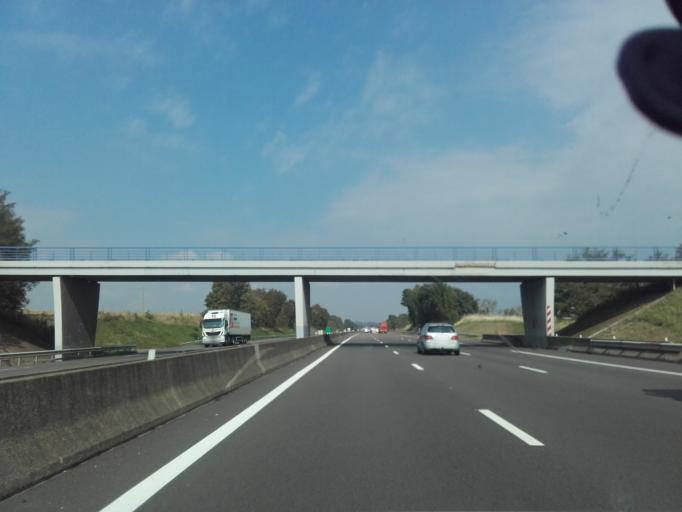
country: FR
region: Rhone-Alpes
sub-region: Departement de l'Ain
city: Pont-de-Vaux
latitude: 46.4649
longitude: 4.8792
